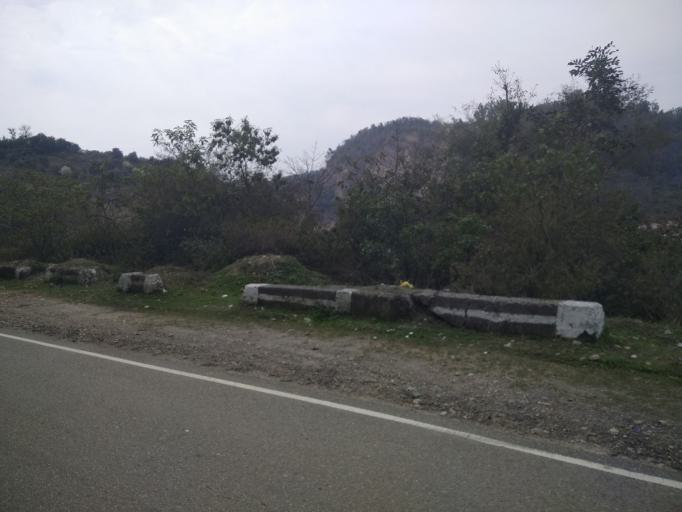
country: IN
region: Himachal Pradesh
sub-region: Kangra
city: Kotla
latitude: 32.2294
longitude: 76.0579
